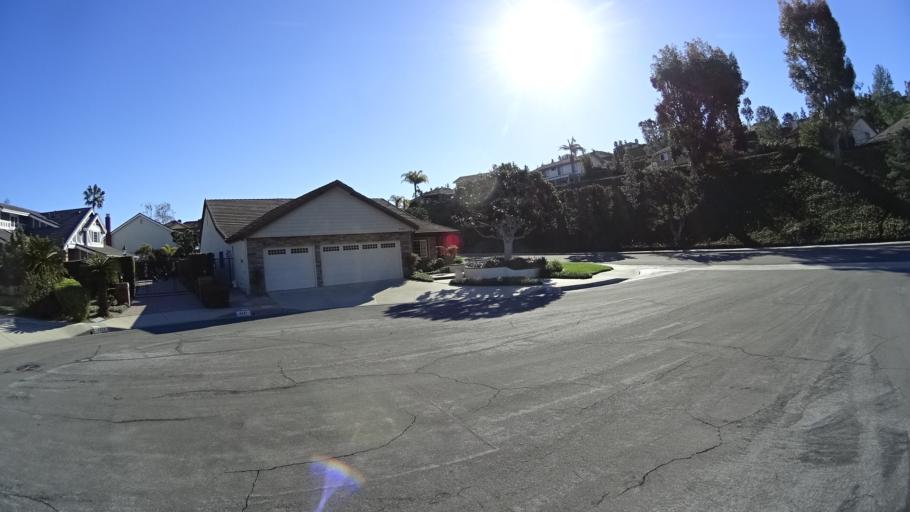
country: US
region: California
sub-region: Orange County
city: Villa Park
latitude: 33.8393
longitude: -117.8178
